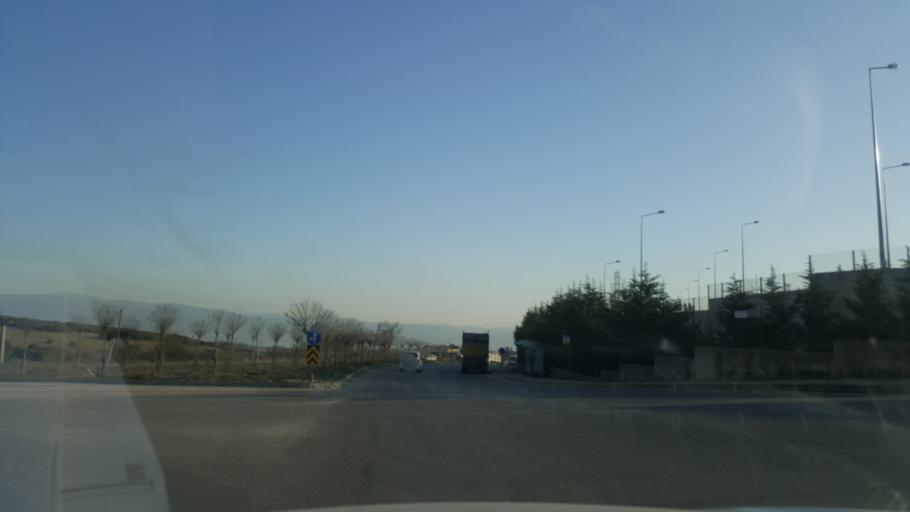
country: TR
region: Kocaeli
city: Tavsancil
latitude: 40.8127
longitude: 29.5670
